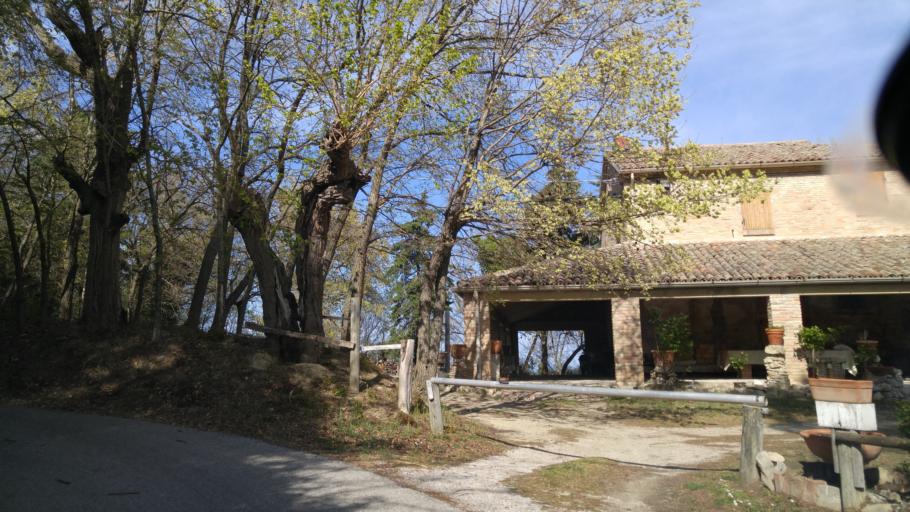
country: IT
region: The Marches
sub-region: Provincia di Pesaro e Urbino
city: Fenile
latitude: 43.8439
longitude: 12.9575
